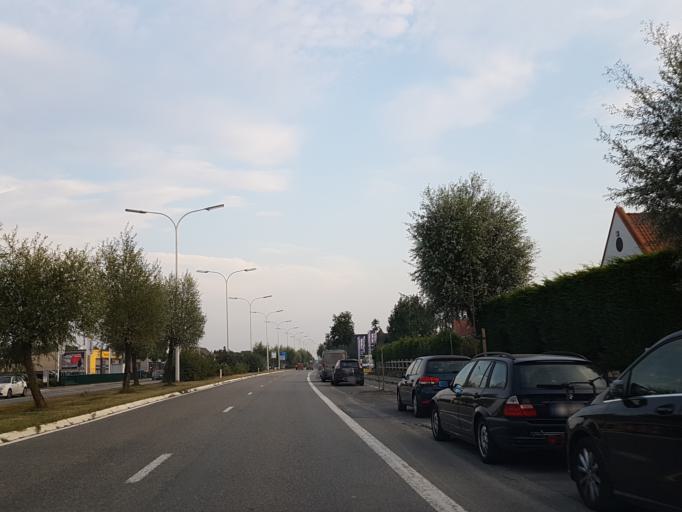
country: BE
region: Flanders
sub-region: Provincie West-Vlaanderen
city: Knokke-Heist
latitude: 51.3287
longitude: 3.2945
